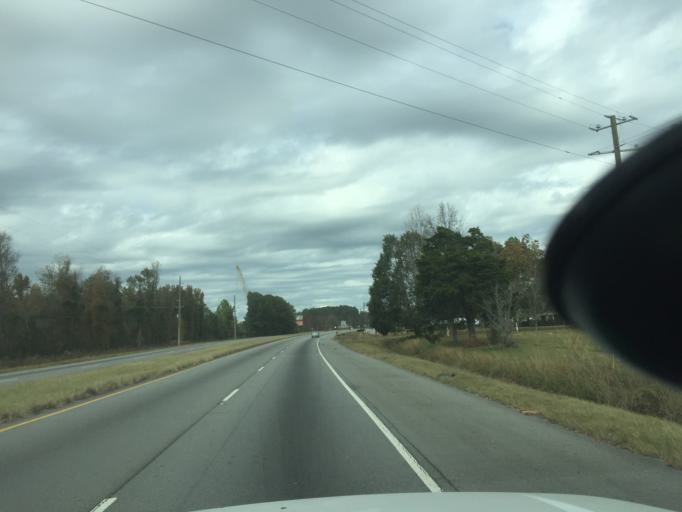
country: US
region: Georgia
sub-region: Chatham County
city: Port Wentworth
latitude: 32.1680
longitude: -81.1860
